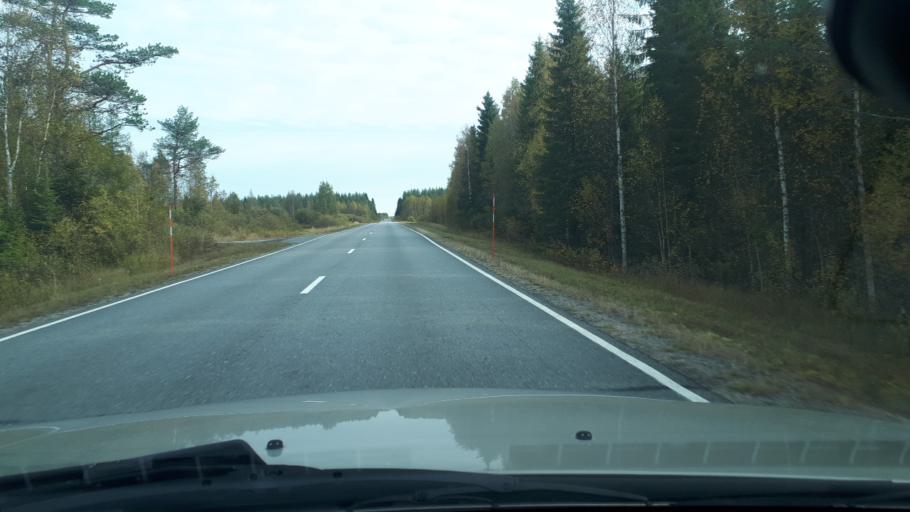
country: FI
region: Lapland
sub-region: Rovaniemi
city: Ranua
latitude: 65.9637
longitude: 26.0777
